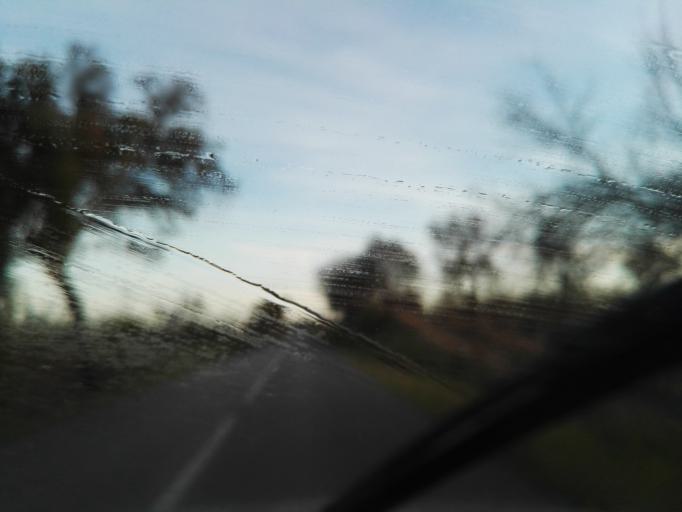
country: PT
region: Evora
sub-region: Montemor-O-Novo
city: Montemor-o-Novo
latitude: 38.7842
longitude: -8.2199
